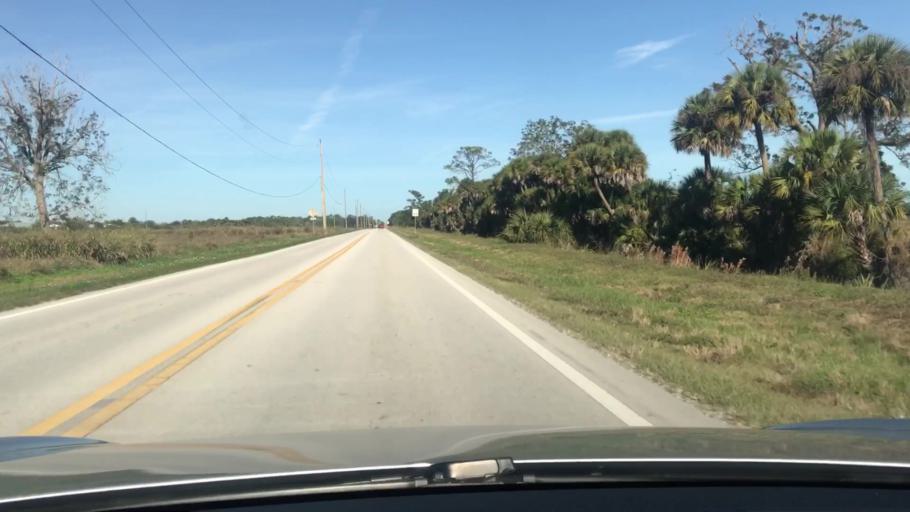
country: US
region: Florida
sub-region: Indian River County
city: Winter Beach
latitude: 27.7047
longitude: -80.4626
